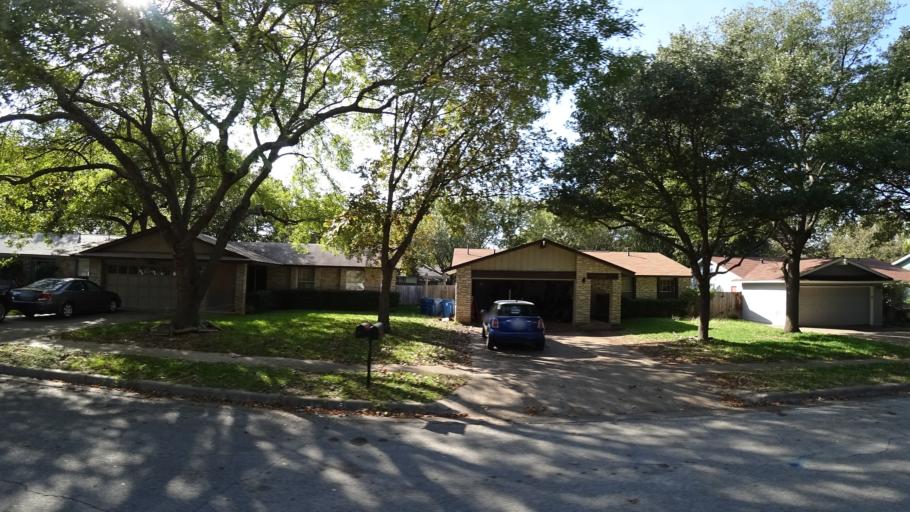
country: US
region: Texas
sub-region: Williamson County
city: Anderson Mill
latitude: 30.4546
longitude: -97.8002
